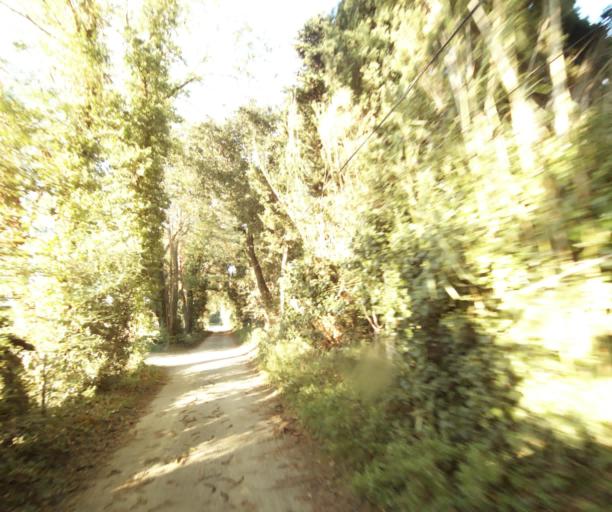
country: FR
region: Languedoc-Roussillon
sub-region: Departement des Pyrenees-Orientales
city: Argelers
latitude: 42.5751
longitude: 3.0120
